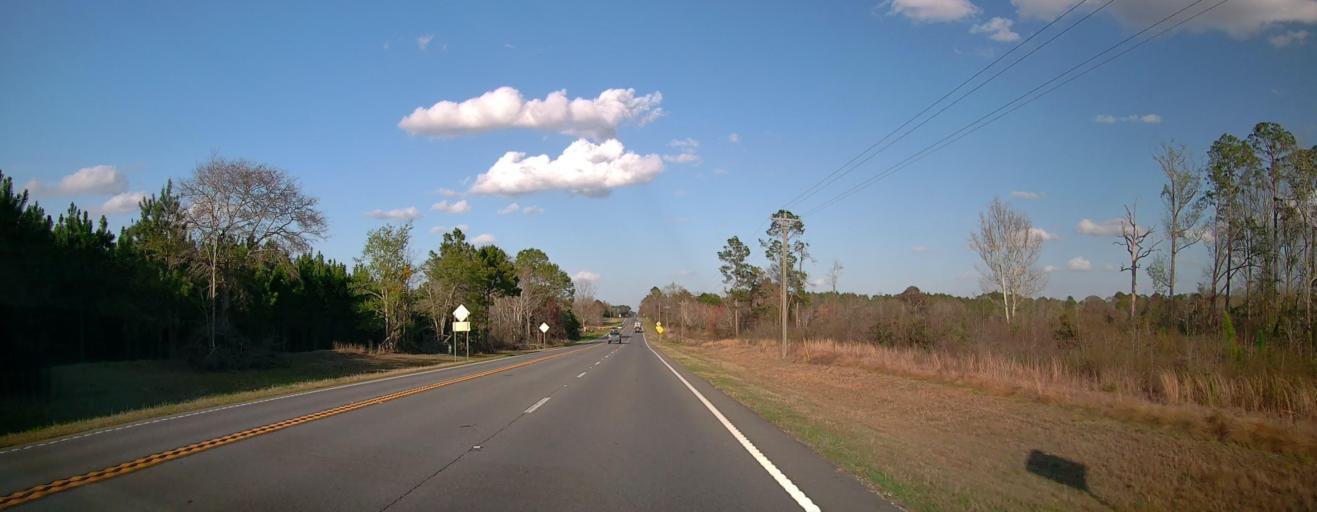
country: US
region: Georgia
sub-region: Tattnall County
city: Reidsville
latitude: 32.1127
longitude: -82.0811
